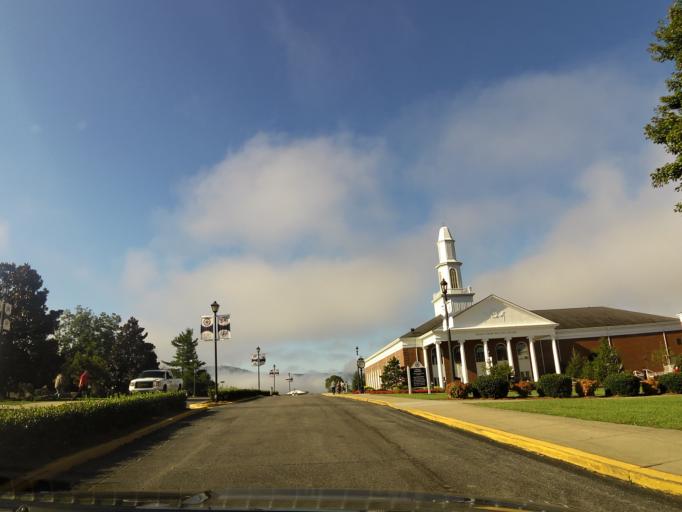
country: US
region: Kentucky
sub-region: Whitley County
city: Williamsburg
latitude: 36.7364
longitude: -84.1616
